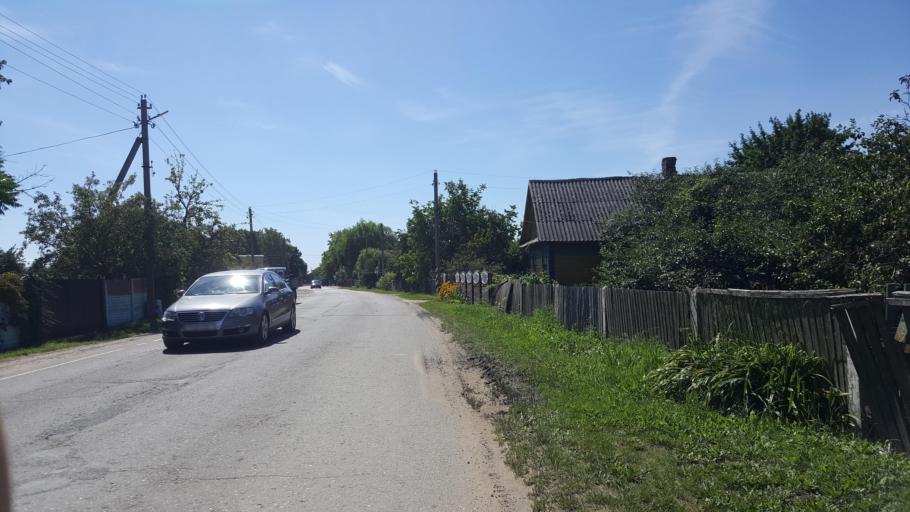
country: BY
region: Brest
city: Charnawchytsy
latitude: 52.2225
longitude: 23.7386
